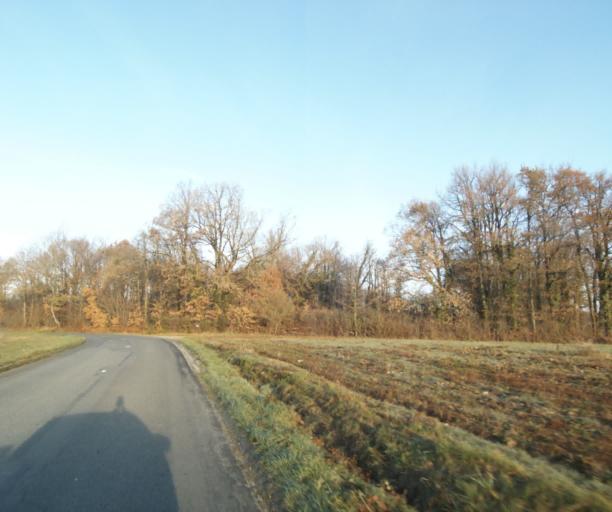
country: FR
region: Poitou-Charentes
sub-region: Departement de la Charente-Maritime
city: Fontcouverte
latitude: 45.7578
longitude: -0.5701
